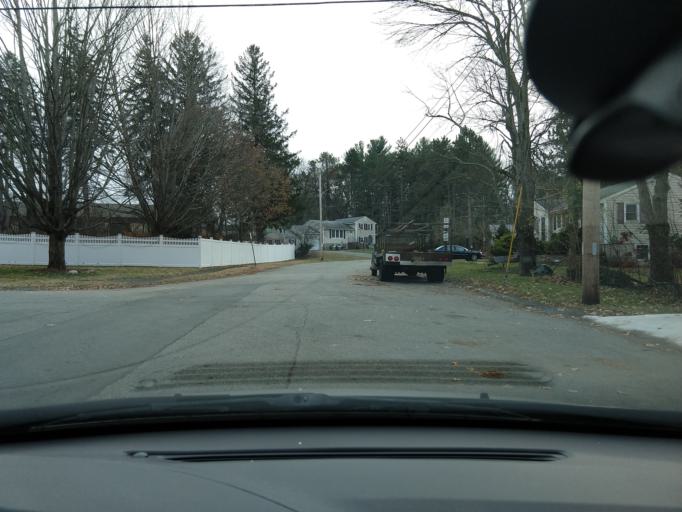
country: US
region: Massachusetts
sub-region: Middlesex County
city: Billerica
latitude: 42.5627
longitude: -71.2758
